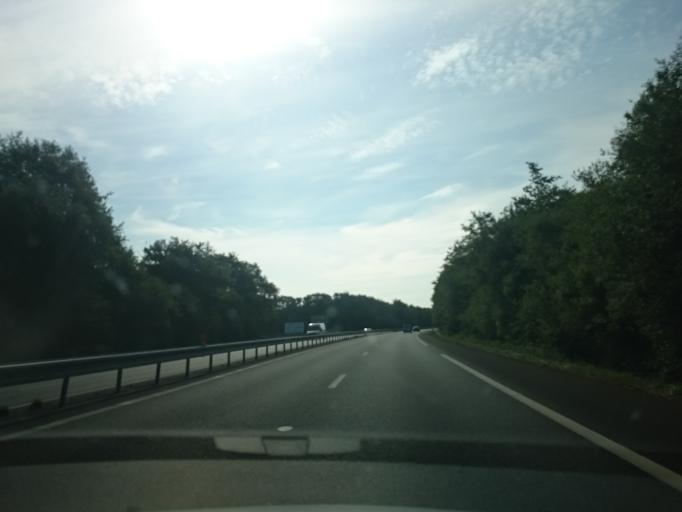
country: FR
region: Brittany
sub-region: Departement du Morbihan
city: Landevant
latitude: 47.7550
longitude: -3.1165
